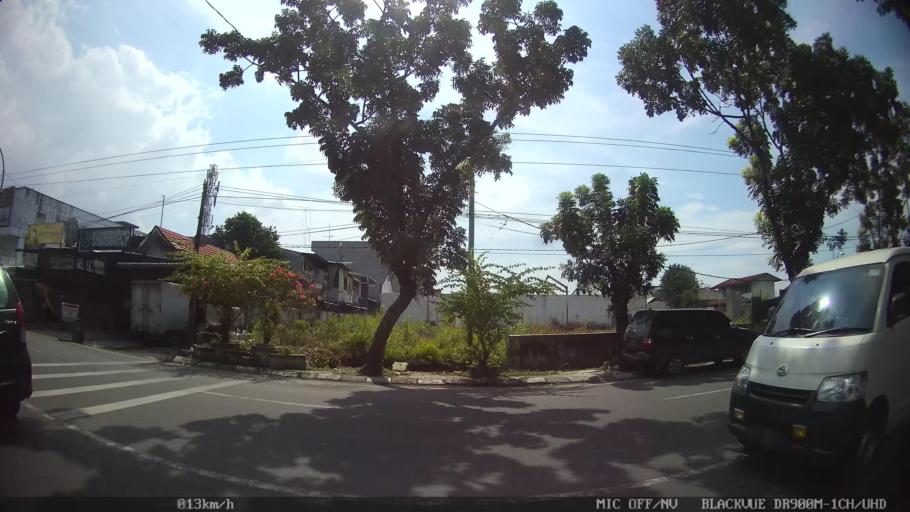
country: ID
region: North Sumatra
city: Medan
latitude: 3.6008
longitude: 98.6690
